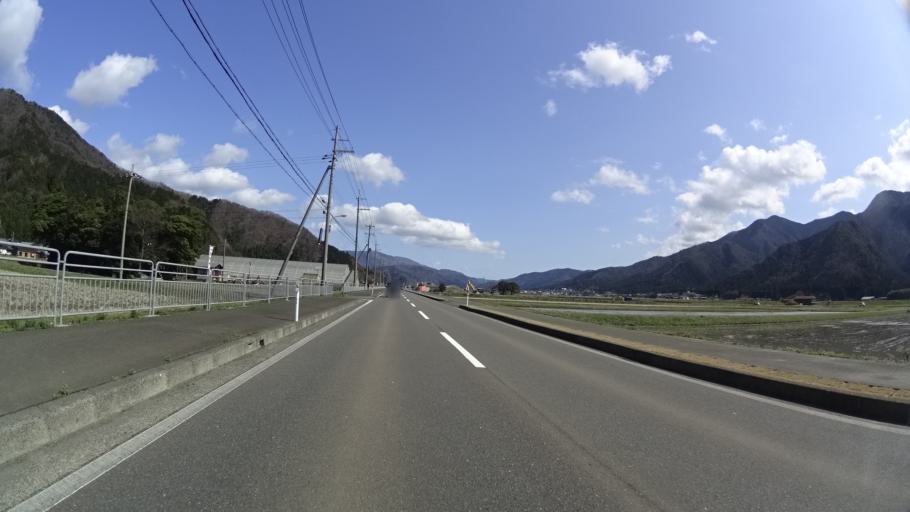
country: JP
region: Fukui
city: Obama
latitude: 35.4736
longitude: 135.8344
